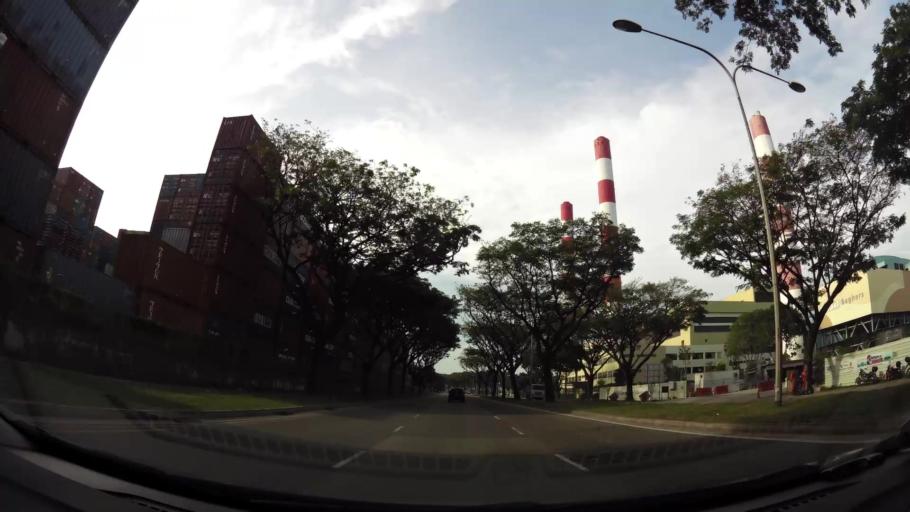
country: MY
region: Johor
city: Johor Bahru
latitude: 1.2980
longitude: 103.6228
